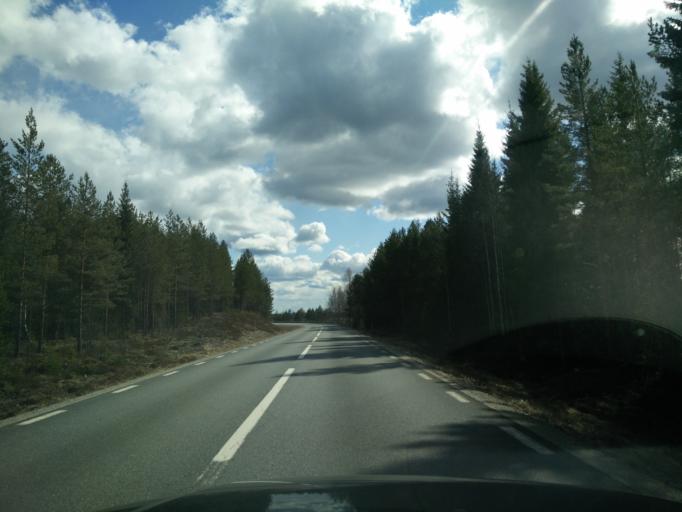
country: SE
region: Jaemtland
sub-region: Braecke Kommun
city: Braecke
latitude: 62.4556
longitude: 14.9682
